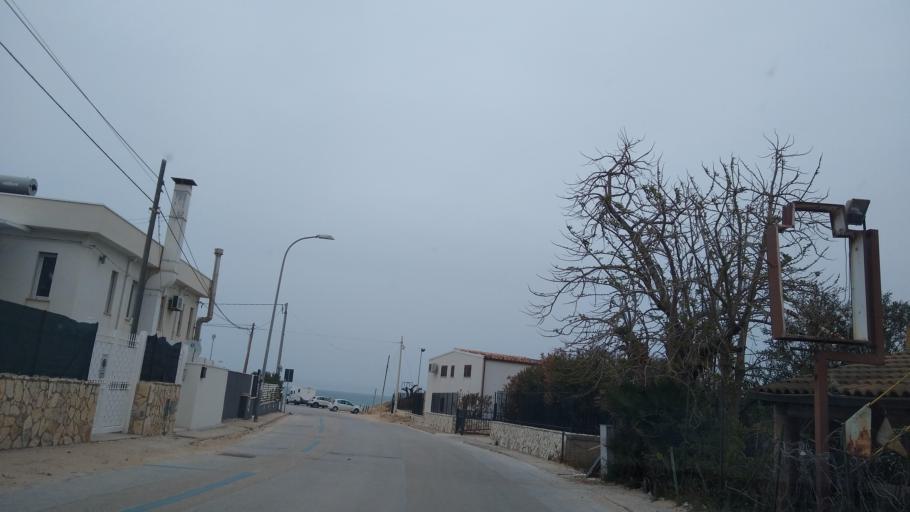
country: IT
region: Sicily
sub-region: Trapani
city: Castellammare del Golfo
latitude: 38.0231
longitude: 12.9038
